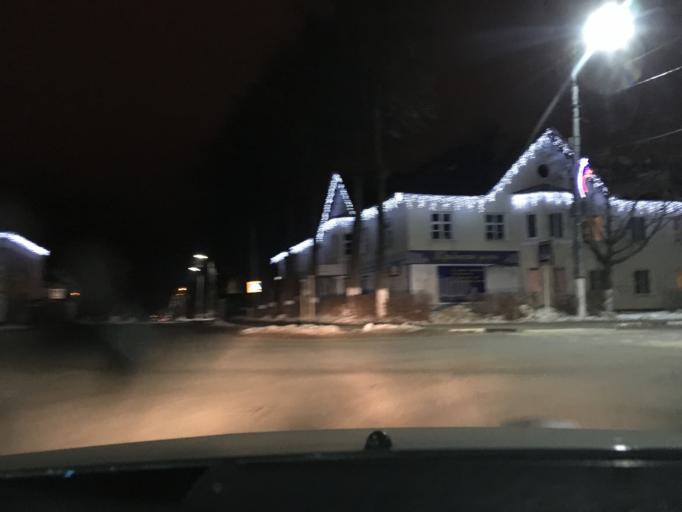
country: RU
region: Tula
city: Pervomayskiy
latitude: 54.0377
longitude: 37.5066
